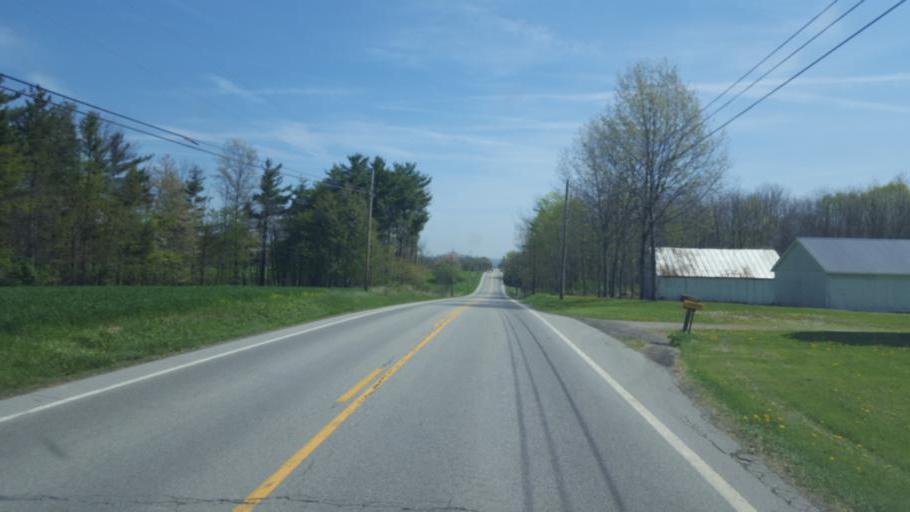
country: US
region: Ohio
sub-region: Wayne County
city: West Salem
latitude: 40.9947
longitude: -82.0771
